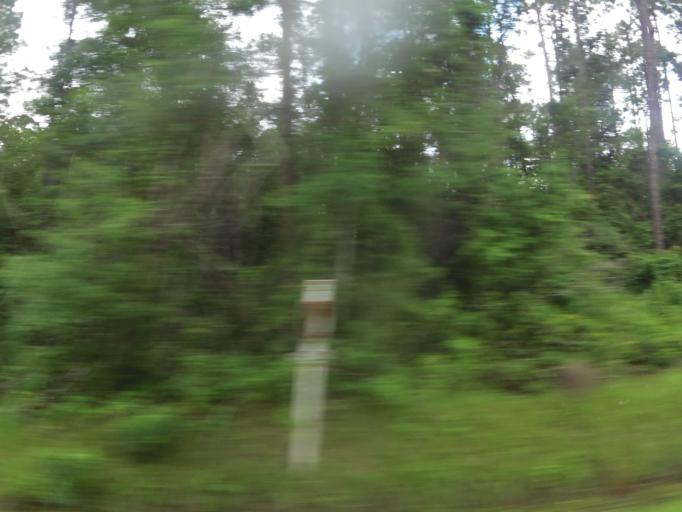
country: US
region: Florida
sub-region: Duval County
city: Baldwin
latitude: 30.3257
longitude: -81.8839
